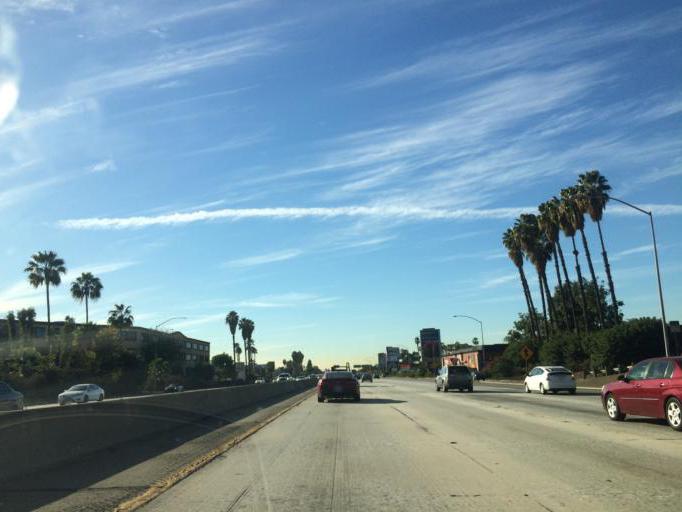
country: US
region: California
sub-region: Los Angeles County
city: Covina
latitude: 34.0719
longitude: -117.8818
